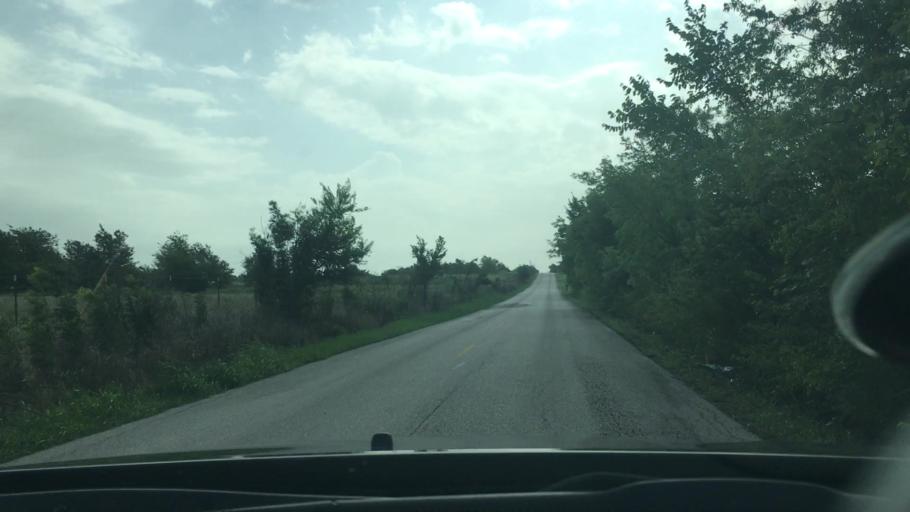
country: US
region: Oklahoma
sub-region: Carter County
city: Lone Grove
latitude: 34.2020
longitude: -97.2231
